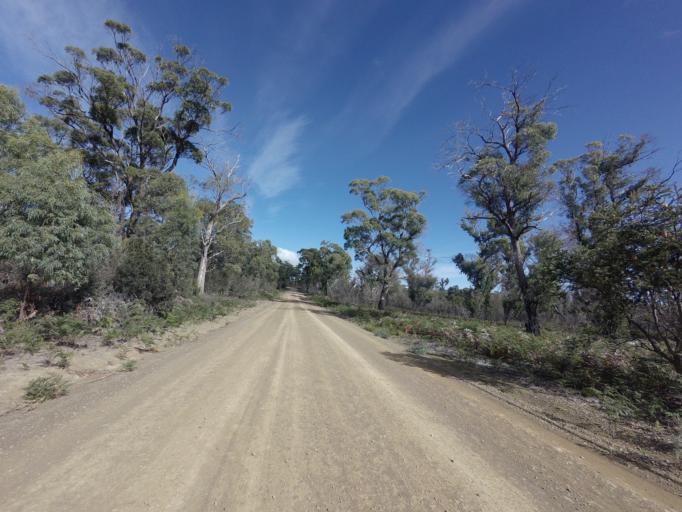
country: AU
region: Tasmania
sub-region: Clarence
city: Sandford
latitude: -42.9784
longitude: 147.7163
